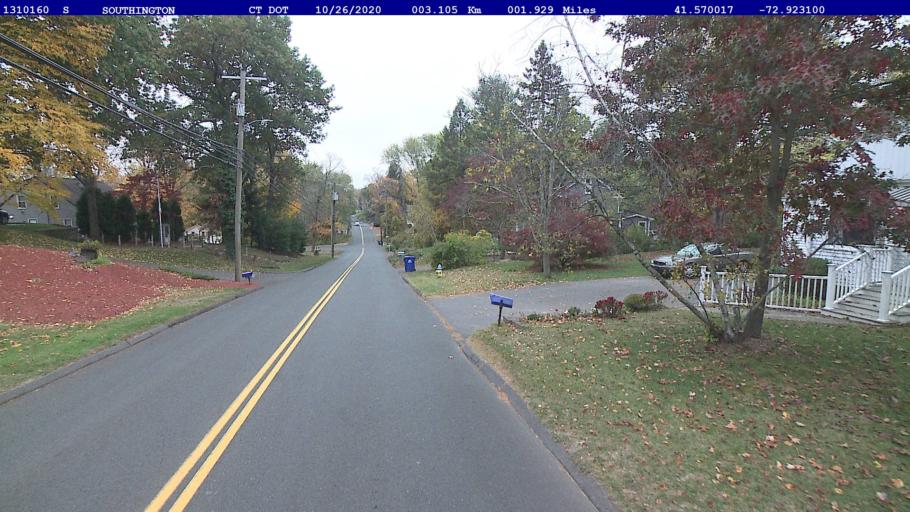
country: US
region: Connecticut
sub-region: New Haven County
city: Wolcott
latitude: 41.5700
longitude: -72.9231
